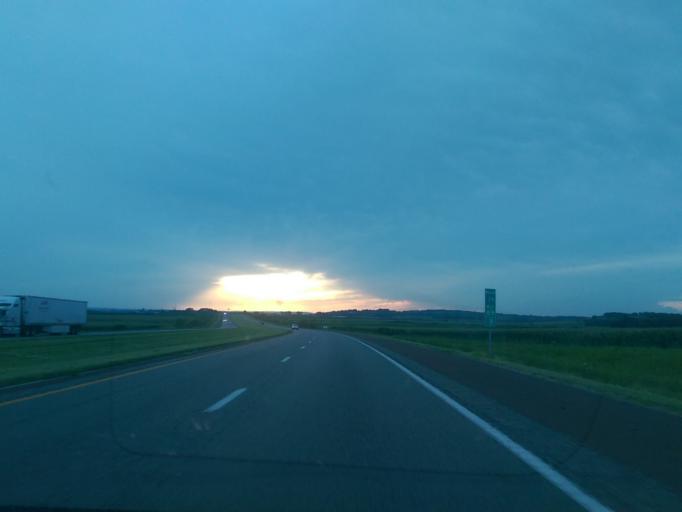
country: US
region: Missouri
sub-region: Holt County
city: Mound City
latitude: 40.1816
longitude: -95.3169
